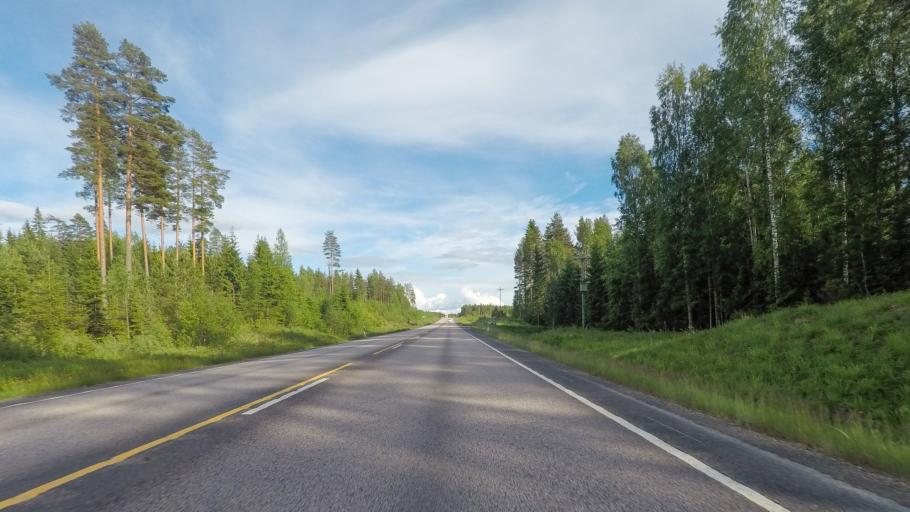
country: FI
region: Central Finland
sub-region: Joutsa
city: Leivonmaeki
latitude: 61.9623
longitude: 26.0905
